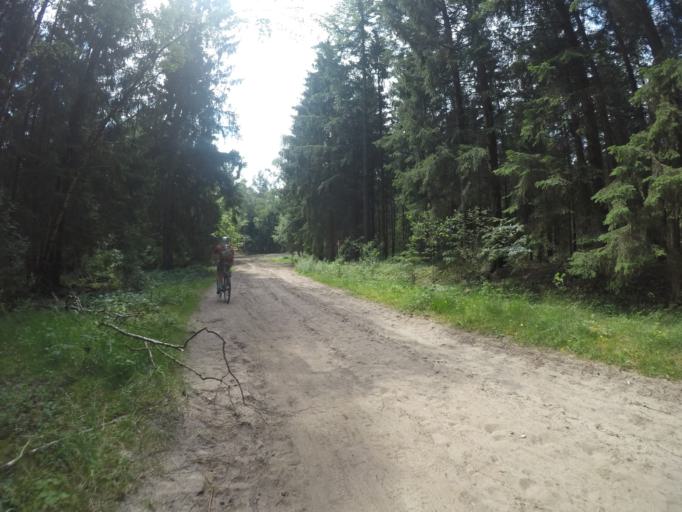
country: DE
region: Lower Saxony
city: Handeloh
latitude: 53.2886
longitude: 9.8449
